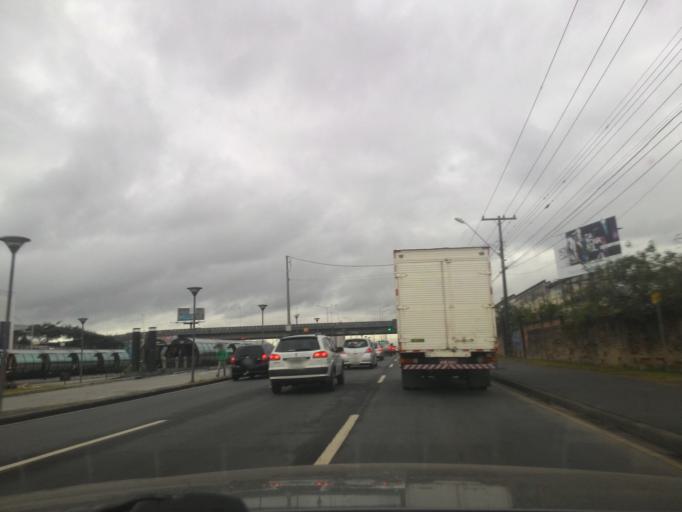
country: BR
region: Parana
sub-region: Curitiba
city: Curitiba
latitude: -25.4973
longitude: -49.2764
